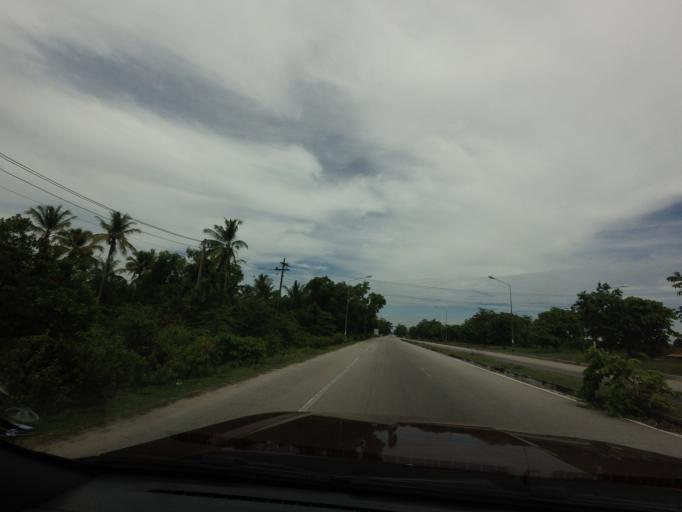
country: TH
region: Narathiwat
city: Narathiwat
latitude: 6.3610
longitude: 101.9154
